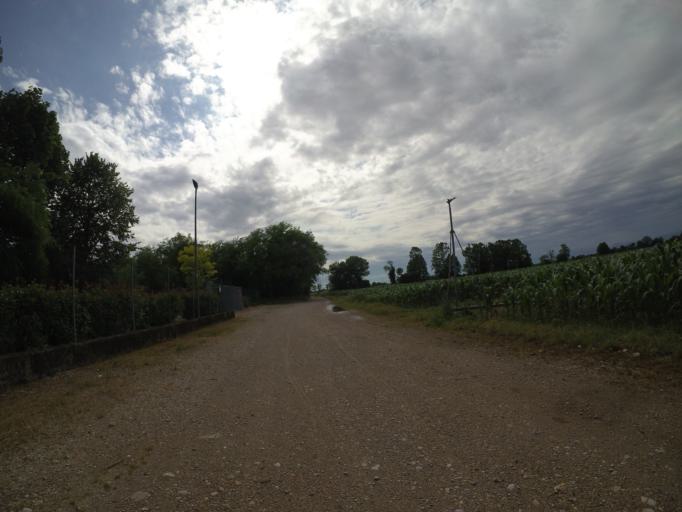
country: IT
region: Friuli Venezia Giulia
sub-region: Provincia di Udine
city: Lestizza
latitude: 45.9674
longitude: 13.1386
